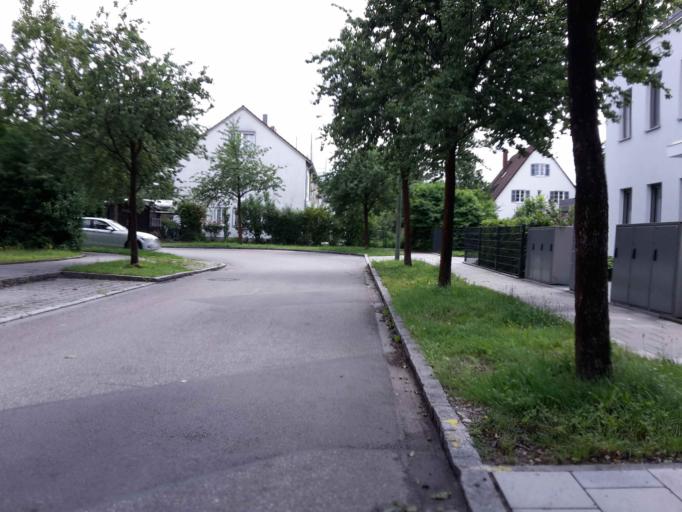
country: DE
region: Bavaria
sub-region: Upper Bavaria
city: Karlsfeld
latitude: 48.1843
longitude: 11.4753
